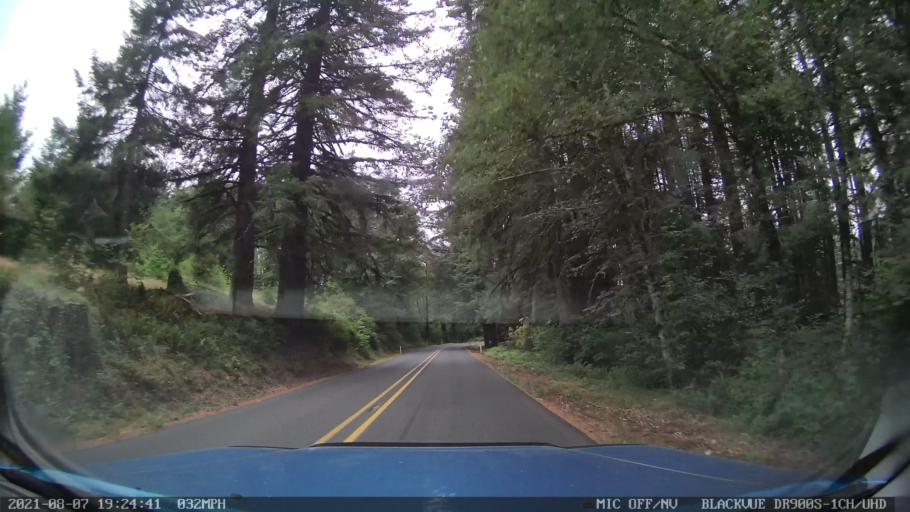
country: US
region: Oregon
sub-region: Linn County
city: Lyons
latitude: 44.8552
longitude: -122.6573
